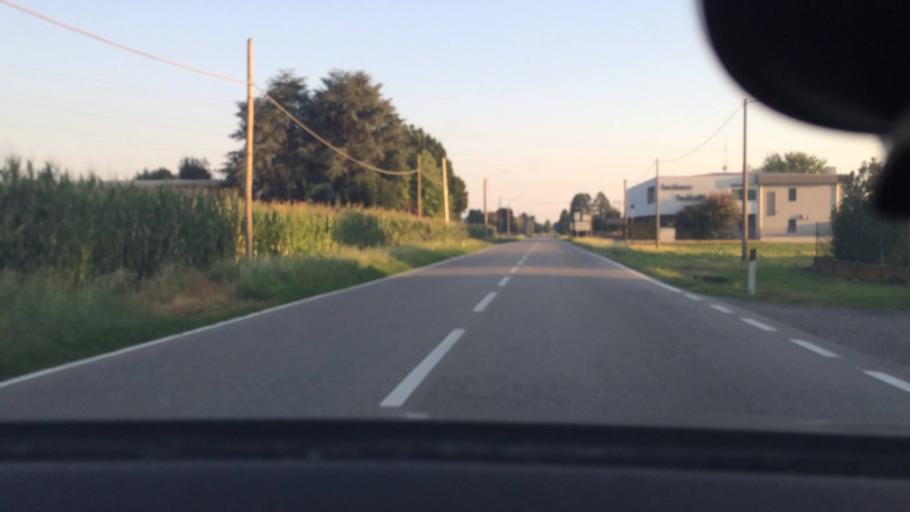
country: IT
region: Lombardy
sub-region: Provincia di Como
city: Turate
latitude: 45.6689
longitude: 9.0018
